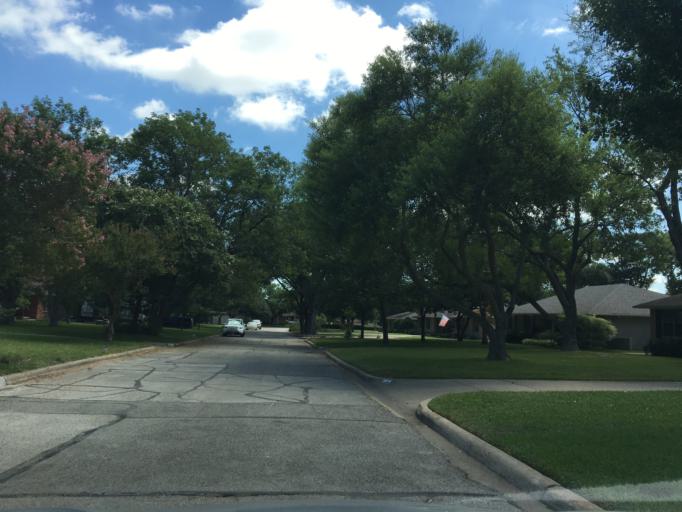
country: US
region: Texas
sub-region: Dallas County
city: Garland
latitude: 32.8412
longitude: -96.6546
